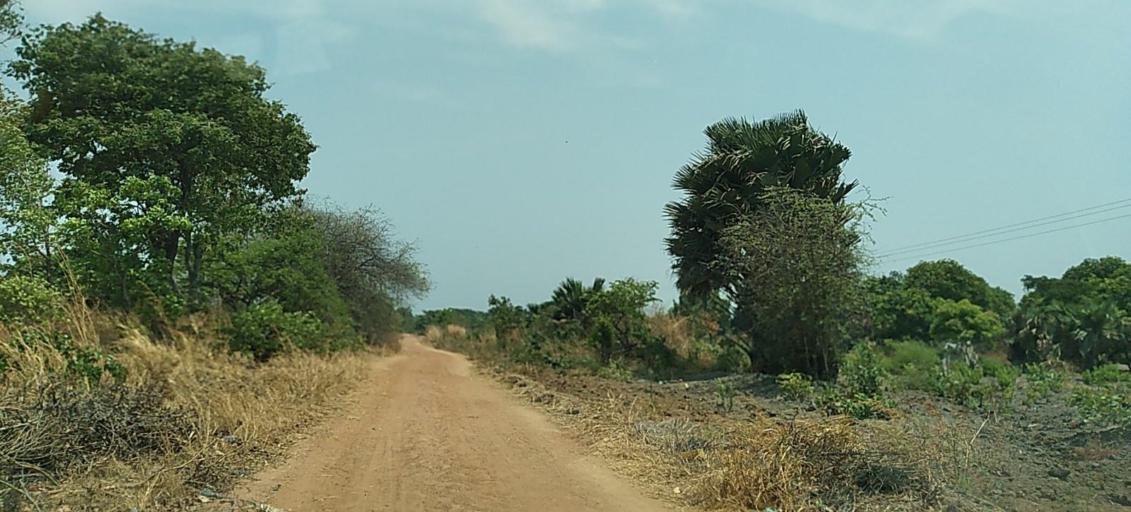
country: ZM
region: Copperbelt
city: Ndola
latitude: -13.0627
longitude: 28.7396
